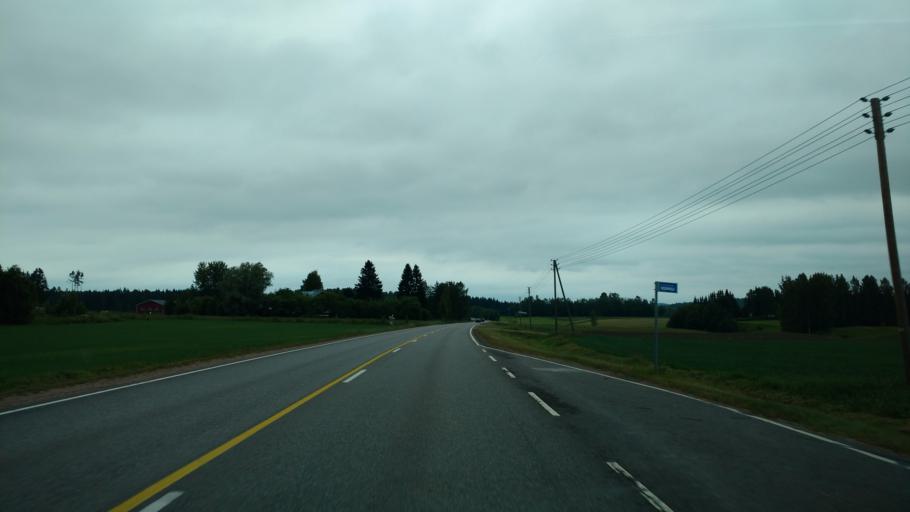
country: FI
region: Varsinais-Suomi
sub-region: Salo
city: Kiikala
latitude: 60.4041
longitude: 23.5834
